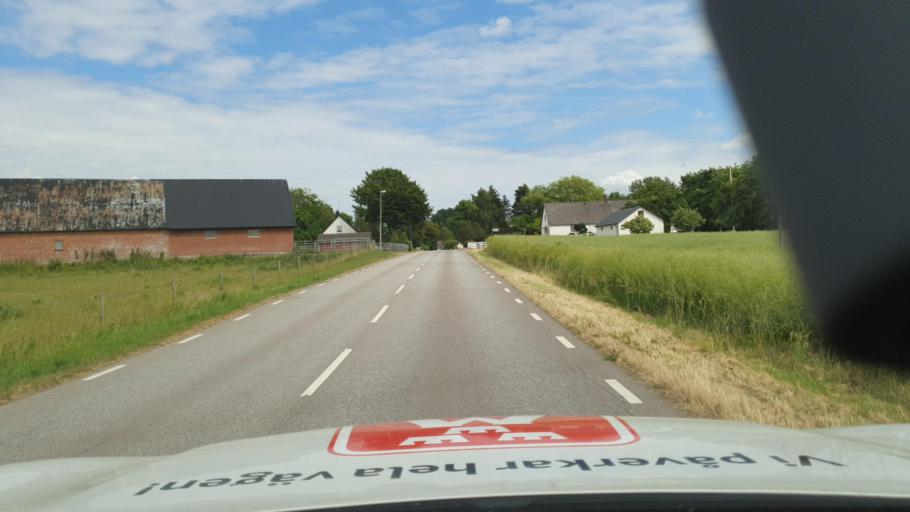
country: SE
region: Skane
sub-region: Svedala Kommun
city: Svedala
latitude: 55.5219
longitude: 13.1827
